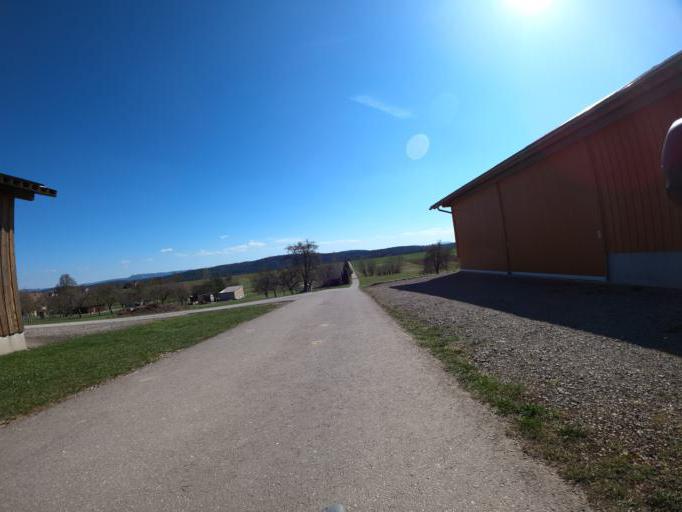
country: DE
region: Baden-Wuerttemberg
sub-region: Tuebingen Region
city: Haigerloch
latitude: 48.3880
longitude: 8.8365
